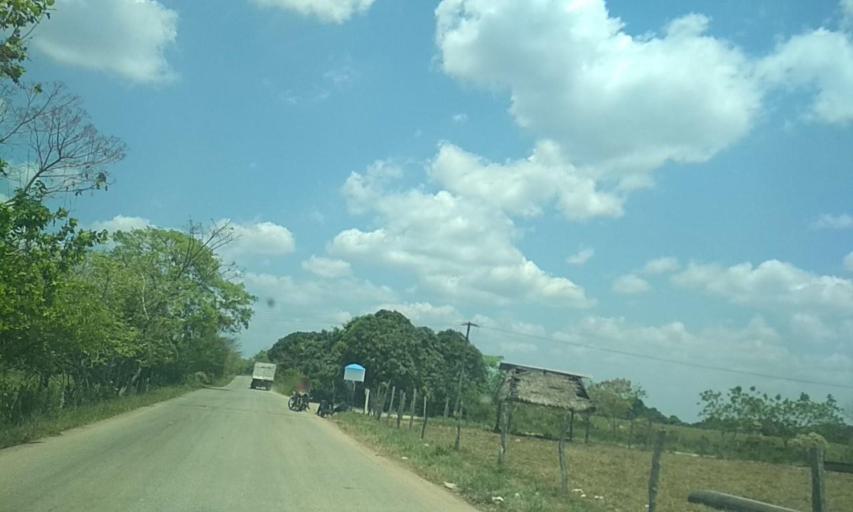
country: MX
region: Tabasco
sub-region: Huimanguillo
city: Francisco Rueda
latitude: 17.7737
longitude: -93.8119
